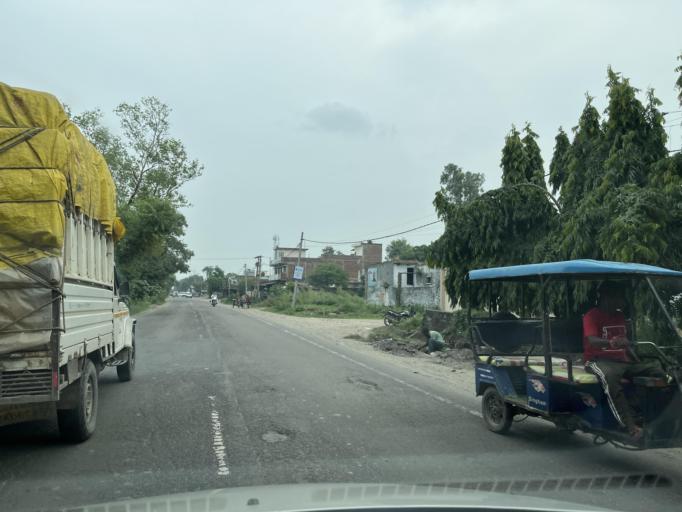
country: IN
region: Uttar Pradesh
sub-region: Rampur
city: Bilaspur
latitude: 29.0329
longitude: 79.2599
